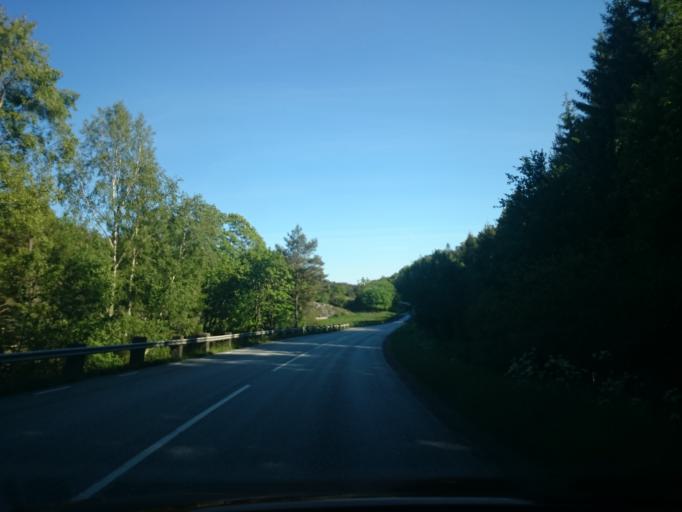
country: SE
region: Vaestra Goetaland
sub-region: Lysekils Kommun
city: Lysekil
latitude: 58.2713
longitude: 11.5342
